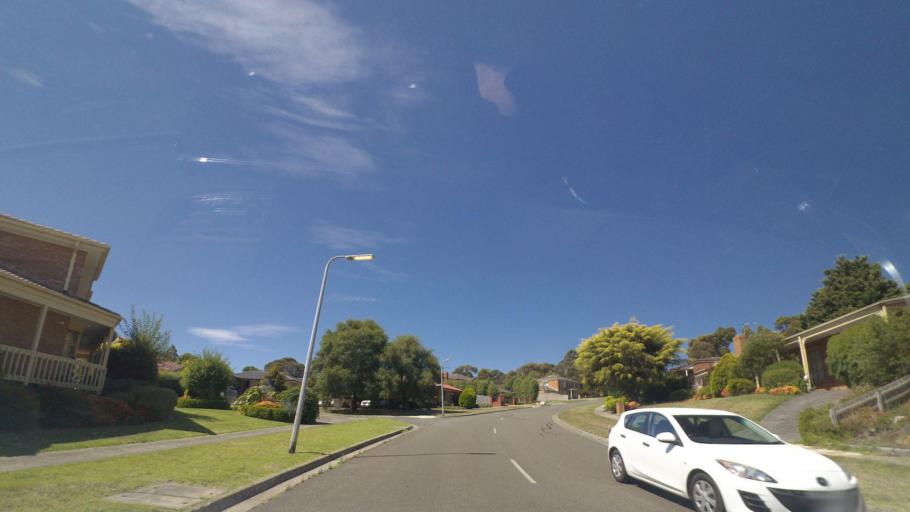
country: AU
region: Victoria
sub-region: Yarra Ranges
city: Lilydale
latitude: -37.7685
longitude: 145.3316
